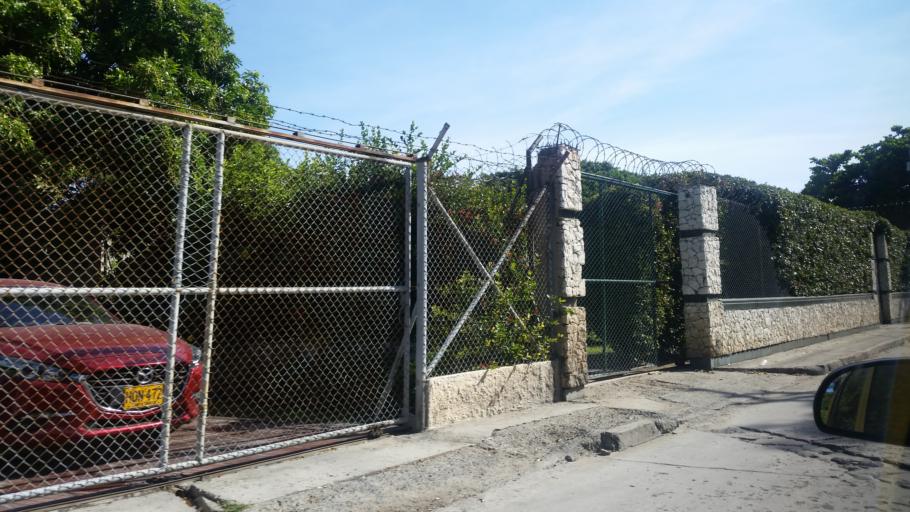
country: CO
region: Magdalena
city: Santa Marta
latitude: 11.2365
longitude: -74.2118
